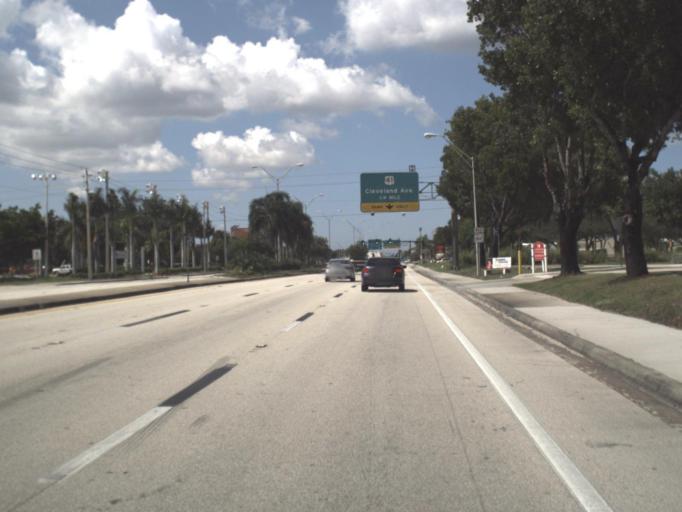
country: US
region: Florida
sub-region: Lee County
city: Pine Manor
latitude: 26.5972
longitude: -81.8637
